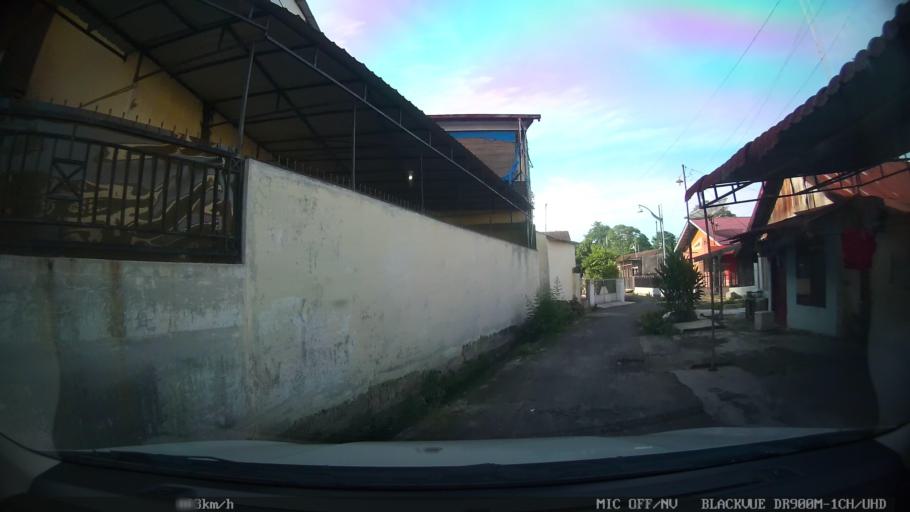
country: ID
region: North Sumatra
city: Medan
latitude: 3.5961
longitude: 98.6706
